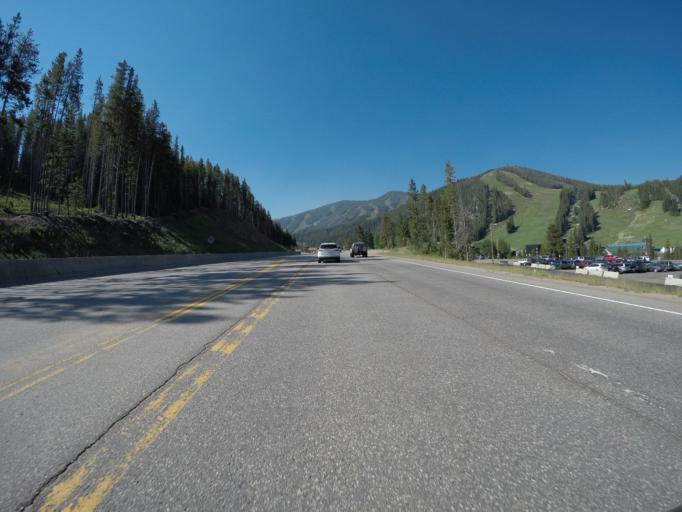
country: US
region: Colorado
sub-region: Grand County
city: Fraser
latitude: 39.8889
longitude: -105.7605
